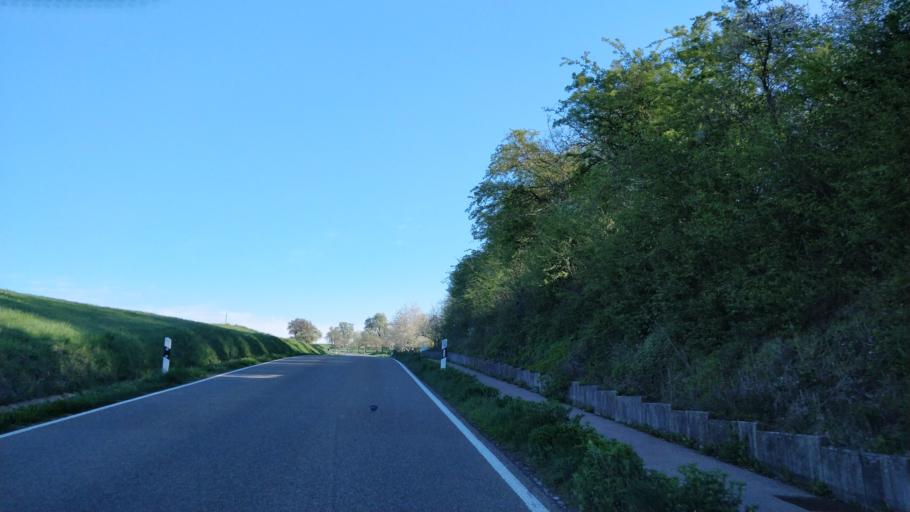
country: DE
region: Baden-Wuerttemberg
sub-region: Regierungsbezirk Stuttgart
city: Michelbach an der Bilz
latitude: 49.0564
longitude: 9.7246
